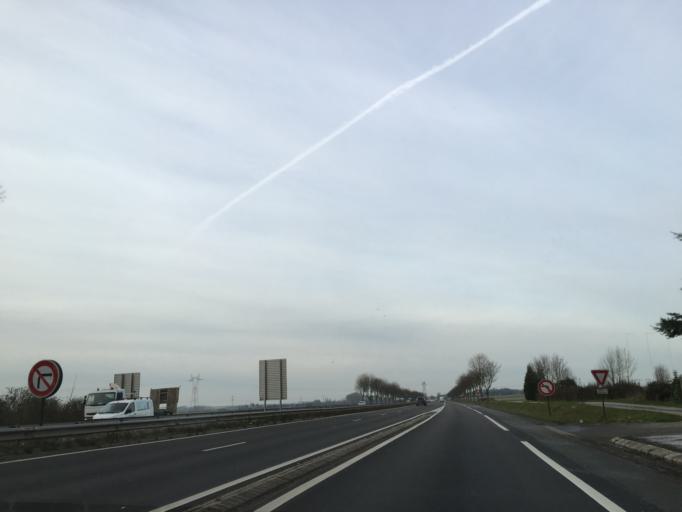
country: FR
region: Nord-Pas-de-Calais
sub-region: Departement du Pas-de-Calais
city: Biache-Saint-Vaast
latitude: 50.3335
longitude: 2.9158
